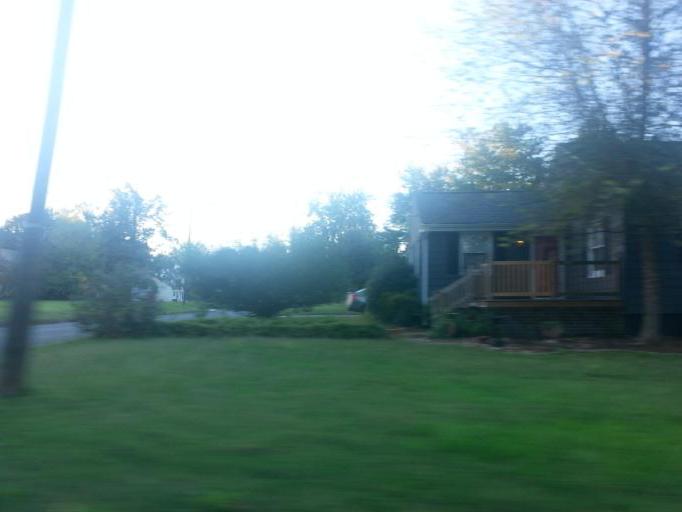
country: US
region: Tennessee
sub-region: Blount County
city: Alcoa
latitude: 35.7778
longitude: -83.9594
